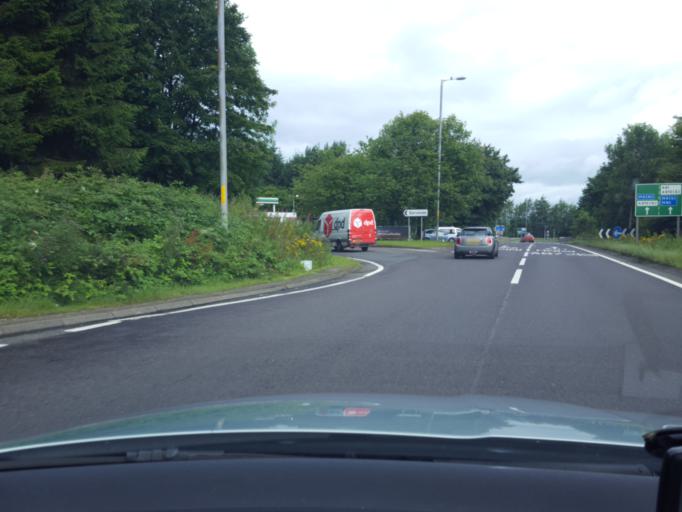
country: GB
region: Scotland
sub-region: Stirling
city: Bannockburn
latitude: 56.0763
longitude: -3.9201
